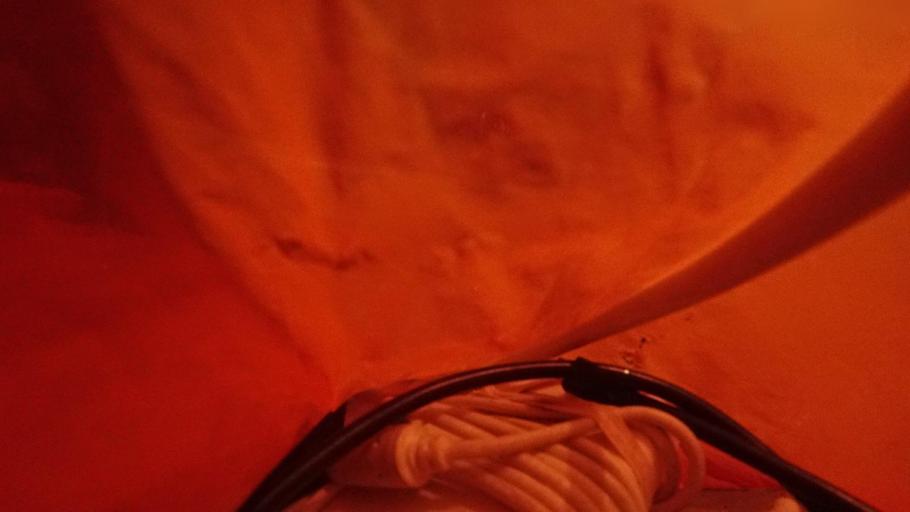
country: RU
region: Jewish Autonomous Oblast
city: Khingansk
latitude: 49.1651
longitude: 130.7951
